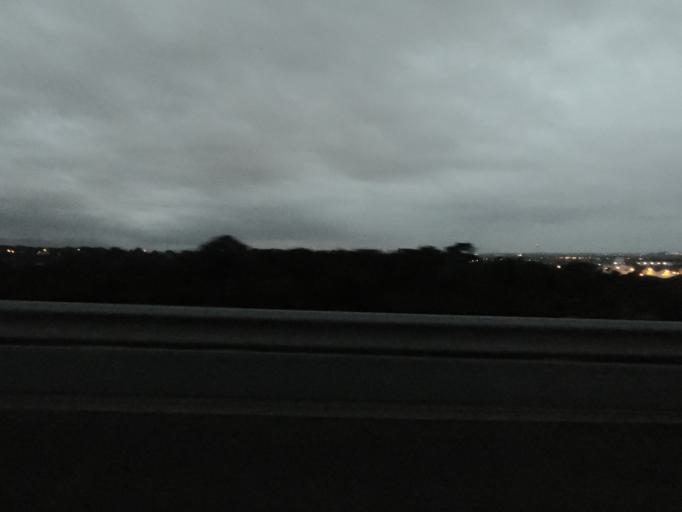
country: PT
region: Setubal
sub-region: Barreiro
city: Santo Antonio da Charneca
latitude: 38.5974
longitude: -9.0318
